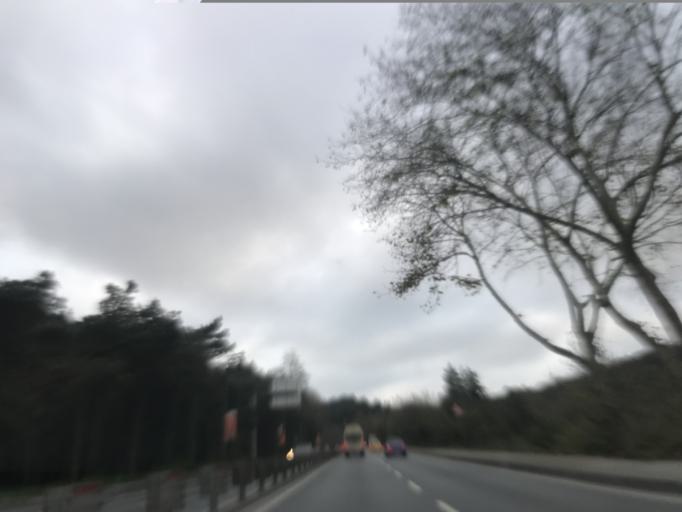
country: TR
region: Istanbul
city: Arikoey
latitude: 41.1495
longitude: 29.0292
